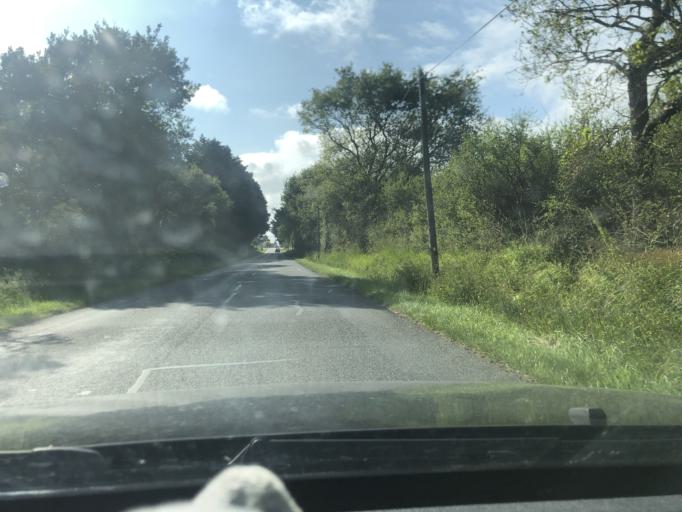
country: FR
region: Brittany
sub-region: Departement du Morbihan
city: Sainte-Helene
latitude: 47.6925
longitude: -3.2375
